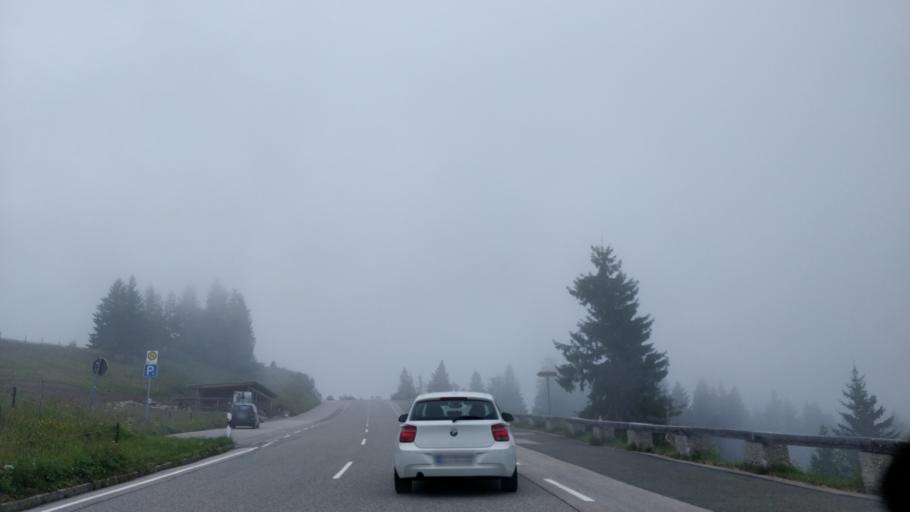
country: AT
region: Salzburg
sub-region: Politischer Bezirk Hallein
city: Kuchl
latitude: 47.6281
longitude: 13.0941
